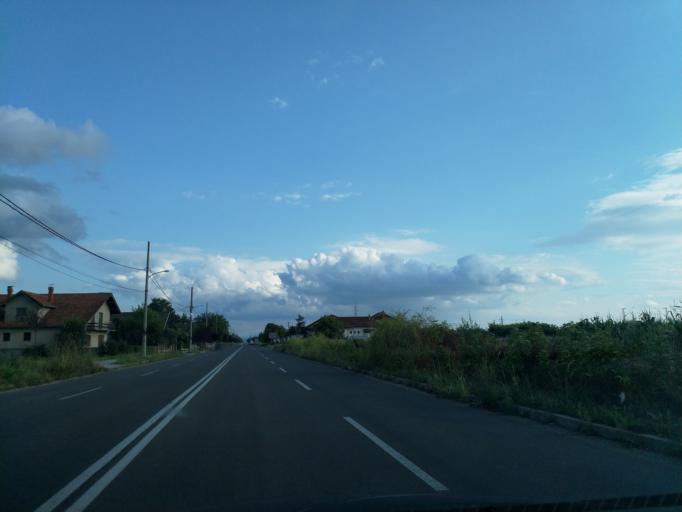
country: RS
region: Central Serbia
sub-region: Pomoravski Okrug
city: Paracin
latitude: 43.8390
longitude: 21.4154
